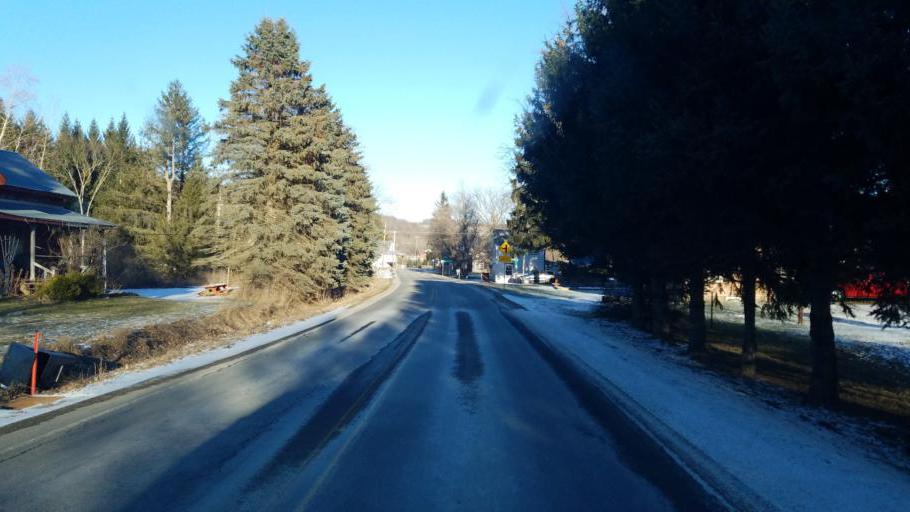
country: US
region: Pennsylvania
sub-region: Tioga County
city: Westfield
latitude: 41.9458
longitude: -77.6895
